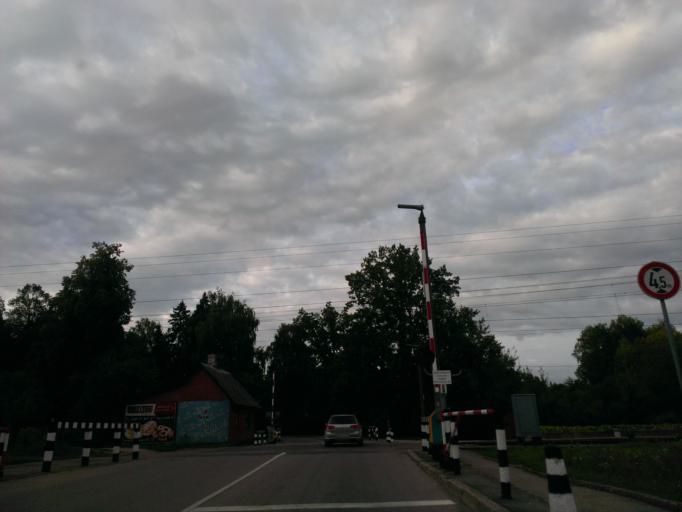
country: LV
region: Ogre
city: Ogre
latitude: 56.8215
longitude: 24.5818
